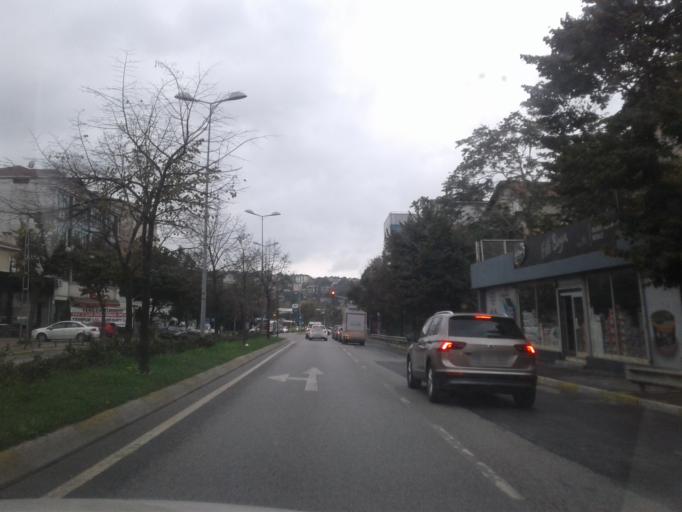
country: TR
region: Istanbul
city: Umraniye
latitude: 41.0818
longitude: 29.0813
